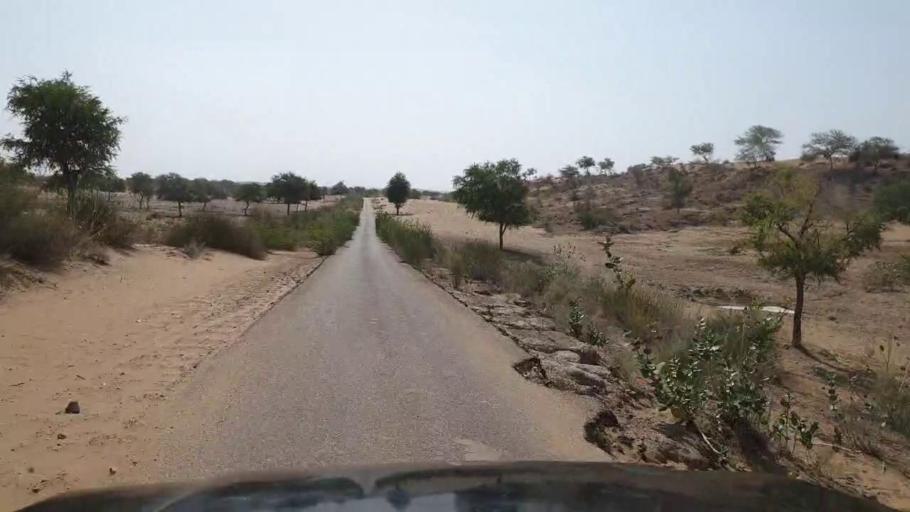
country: PK
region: Sindh
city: Islamkot
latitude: 24.9224
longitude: 70.1276
